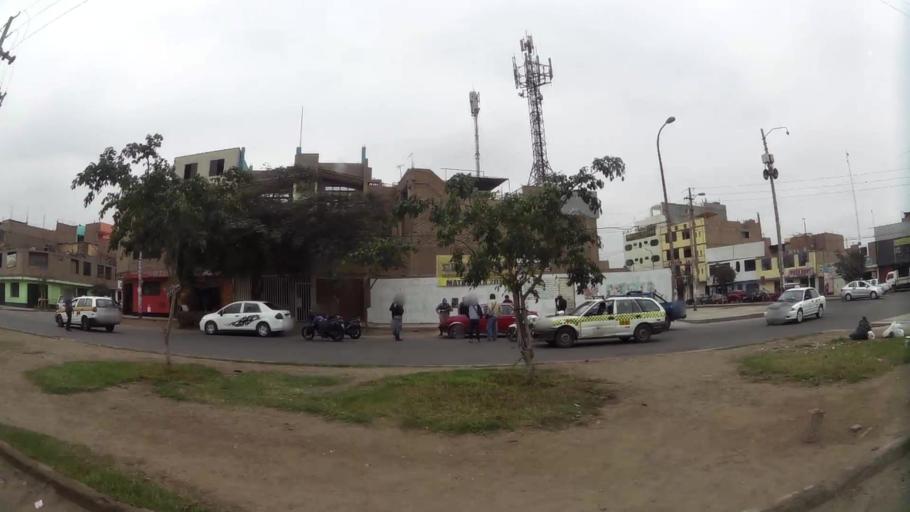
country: PE
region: Lima
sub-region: Lima
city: Independencia
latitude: -11.9822
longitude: -77.0858
